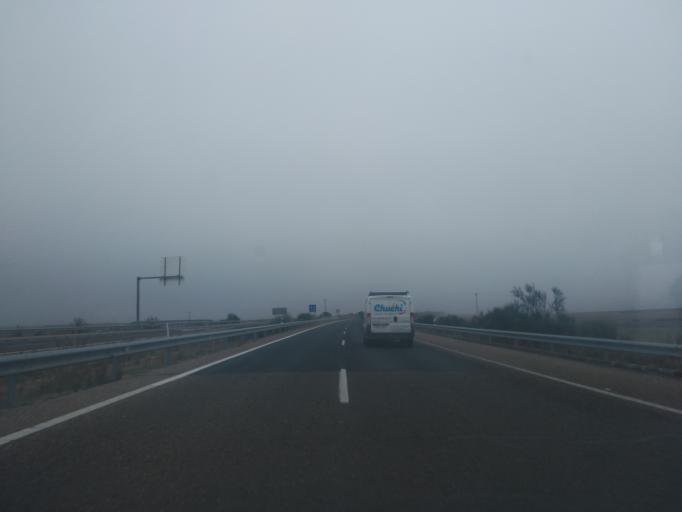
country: ES
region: Castille and Leon
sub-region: Provincia de Salamanca
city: Pajares de la Laguna
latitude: 41.0958
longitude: -5.5015
